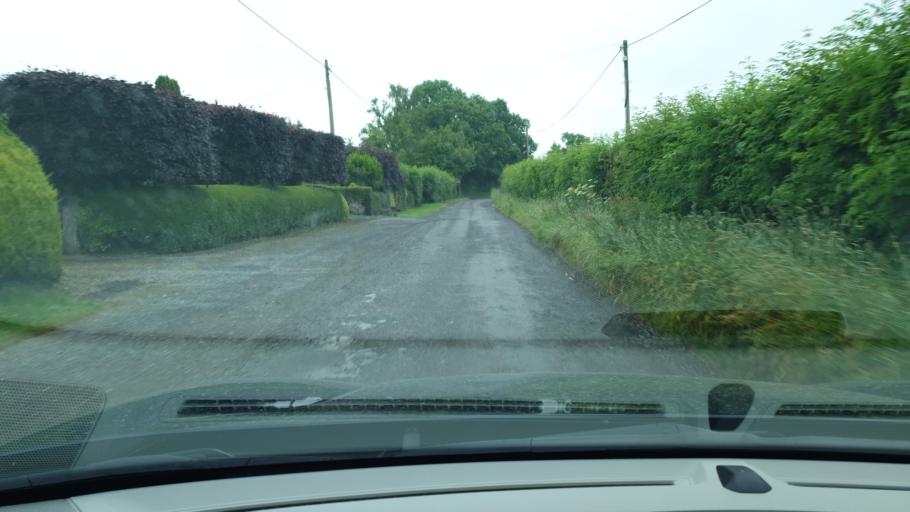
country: IE
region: Leinster
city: Hartstown
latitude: 53.4464
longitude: -6.4283
